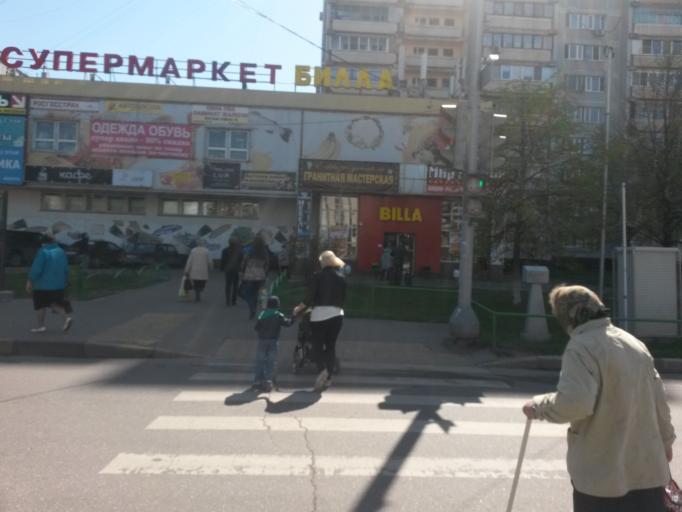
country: RU
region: Moscow
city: Mar'ino
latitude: 55.6463
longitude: 37.7205
